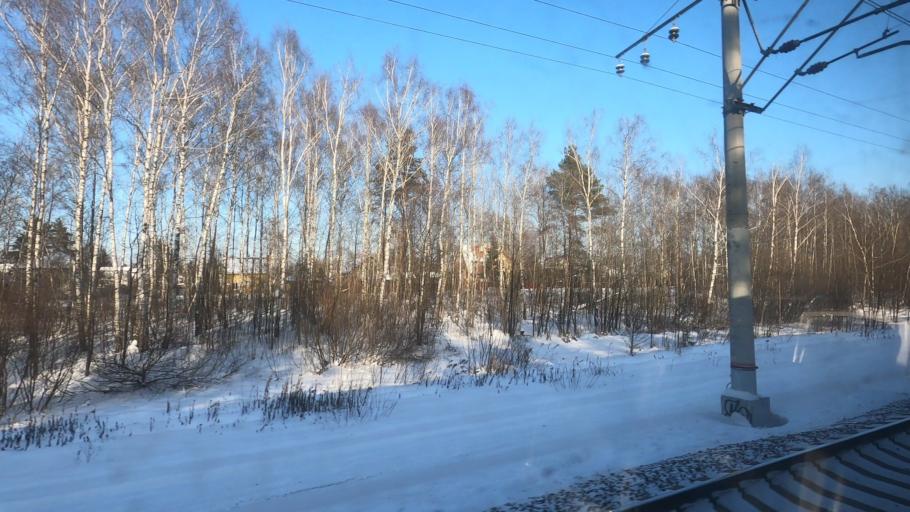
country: RU
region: Moskovskaya
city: Imeni Vorovskogo
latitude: 55.7219
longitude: 38.3051
